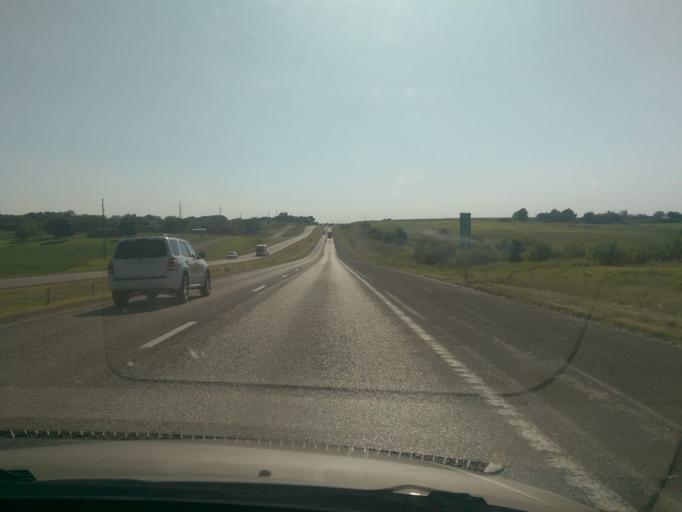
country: US
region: Missouri
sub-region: Lafayette County
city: Concordia
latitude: 38.9929
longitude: -93.6042
